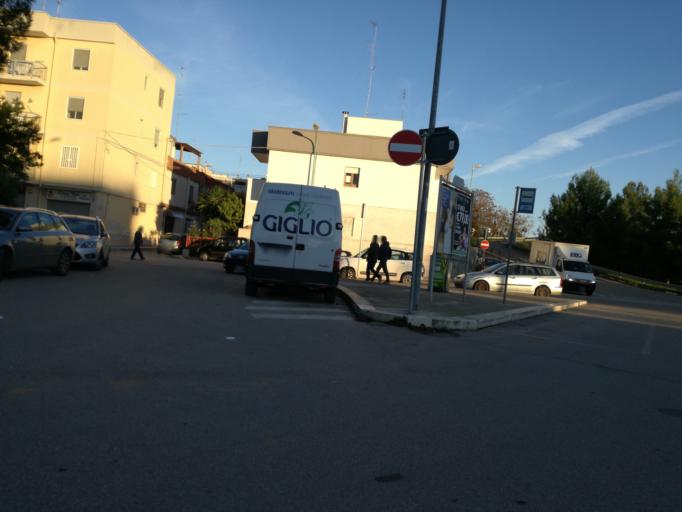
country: IT
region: Apulia
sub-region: Provincia di Bari
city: Adelfia
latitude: 40.9987
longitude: 16.8734
